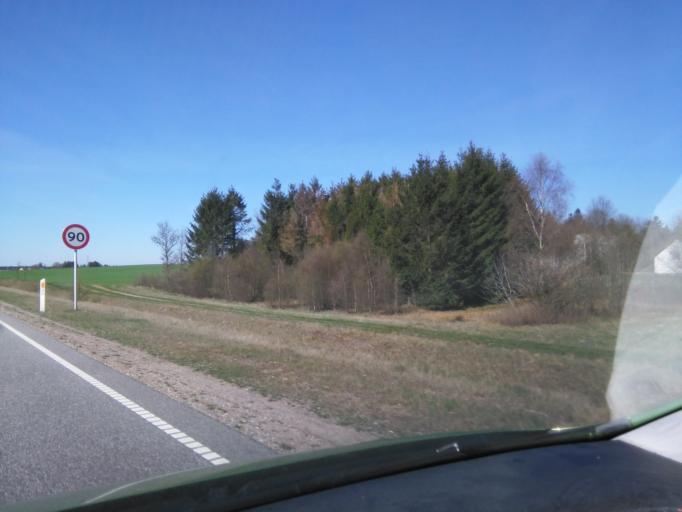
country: DK
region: South Denmark
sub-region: Vejle Kommune
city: Give
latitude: 55.7928
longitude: 9.1882
